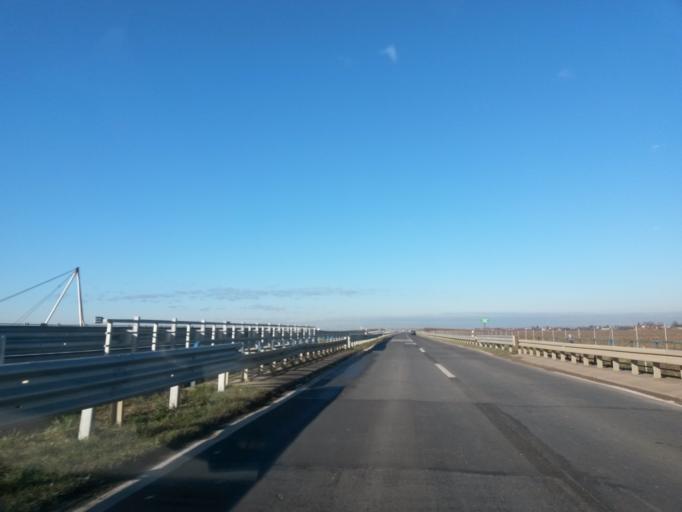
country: HR
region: Osjecko-Baranjska
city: Visnjevac
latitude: 45.5603
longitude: 18.6009
